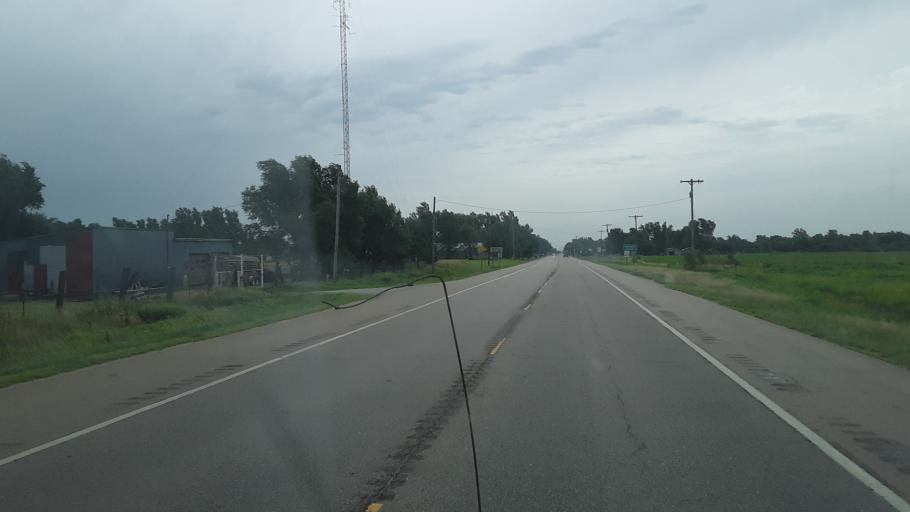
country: US
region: Kansas
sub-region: Stafford County
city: Saint John
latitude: 37.9566
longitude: -98.9780
